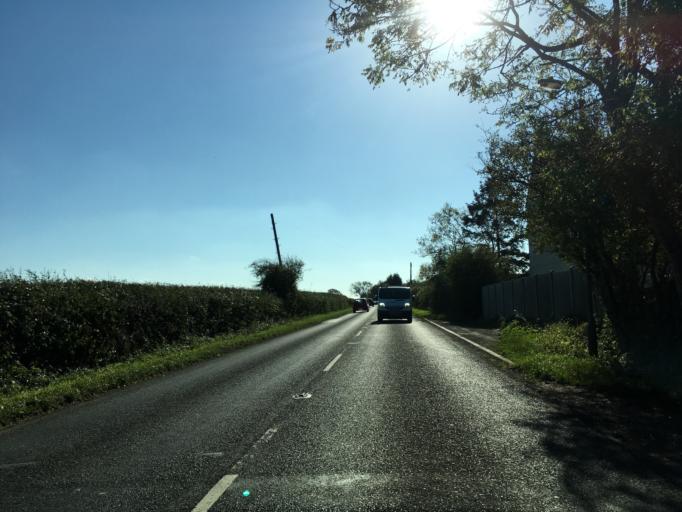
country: GB
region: England
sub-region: South Gloucestershire
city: Wickwar
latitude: 51.5808
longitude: -2.3996
